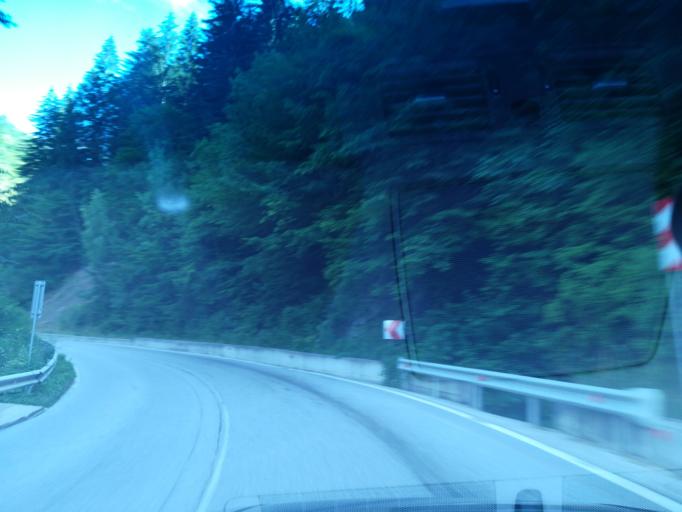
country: BG
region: Smolyan
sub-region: Obshtina Chepelare
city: Chepelare
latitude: 41.7799
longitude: 24.7069
